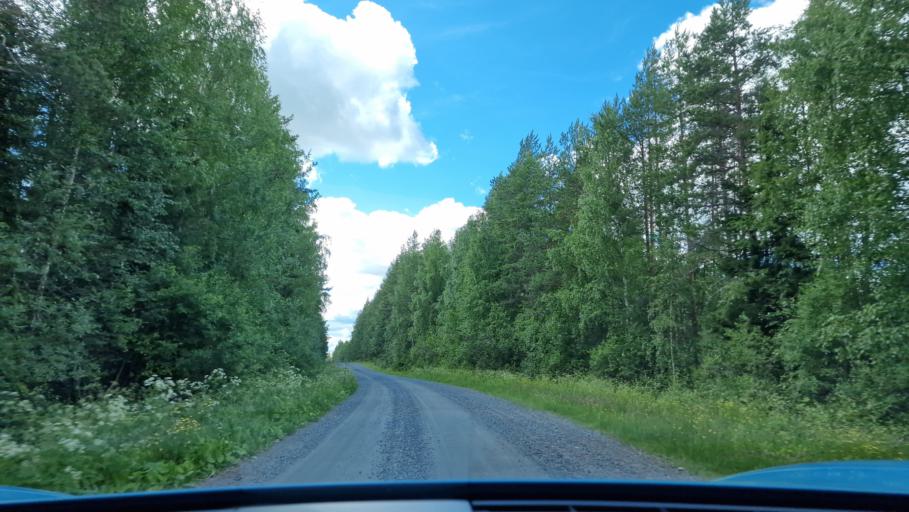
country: FI
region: Southern Ostrobothnia
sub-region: Jaerviseutu
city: Soini
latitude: 62.8490
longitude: 24.3483
